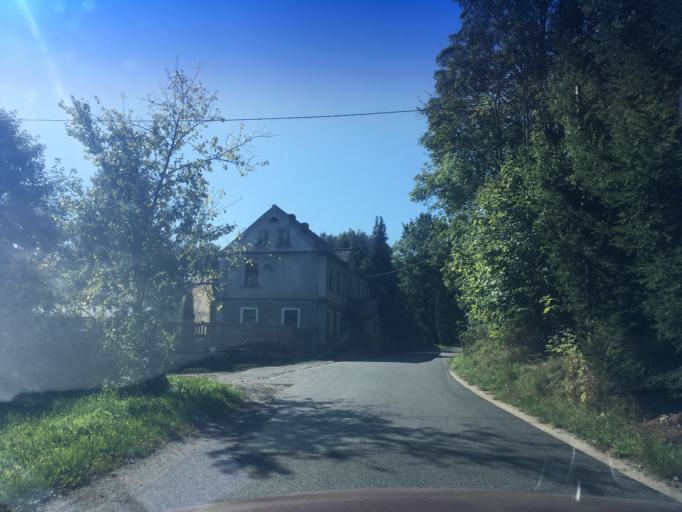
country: PL
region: Lower Silesian Voivodeship
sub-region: Powiat lubanski
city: Lesna
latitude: 51.0126
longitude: 15.1995
